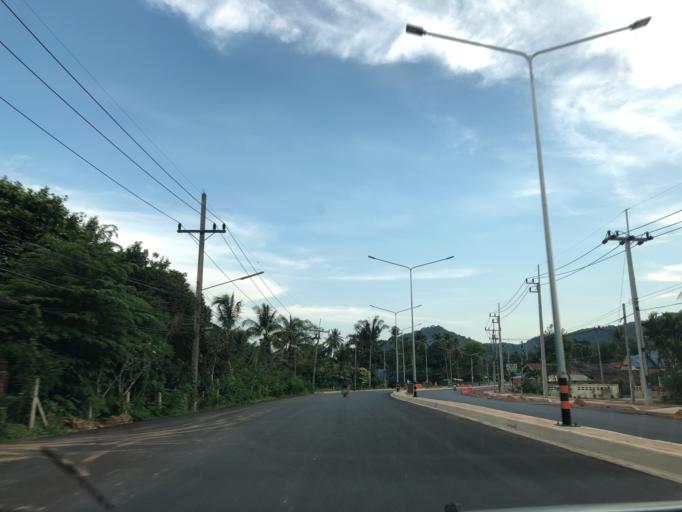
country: TH
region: Phangnga
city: Ban Ao Nang
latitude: 8.0624
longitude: 98.8421
